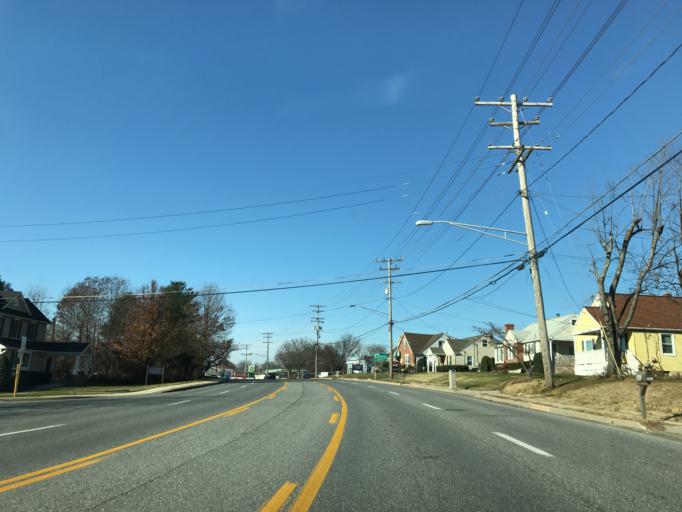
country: US
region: Maryland
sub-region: Baltimore County
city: Carney
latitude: 39.3983
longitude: -76.5334
